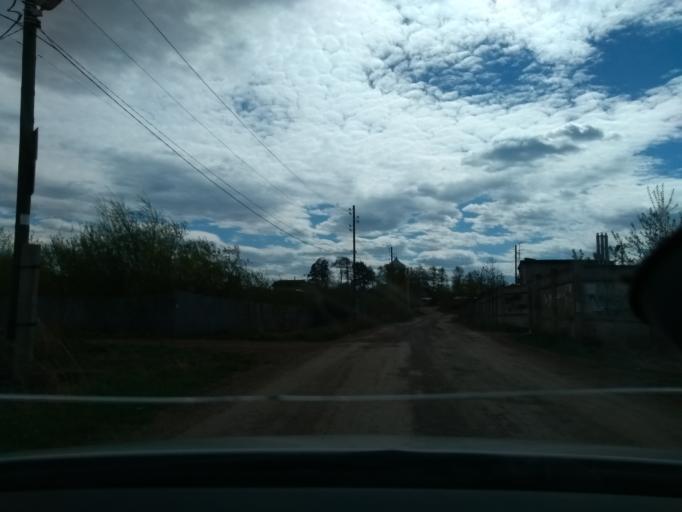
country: RU
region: Perm
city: Lobanovo
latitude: 57.8636
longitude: 56.3031
